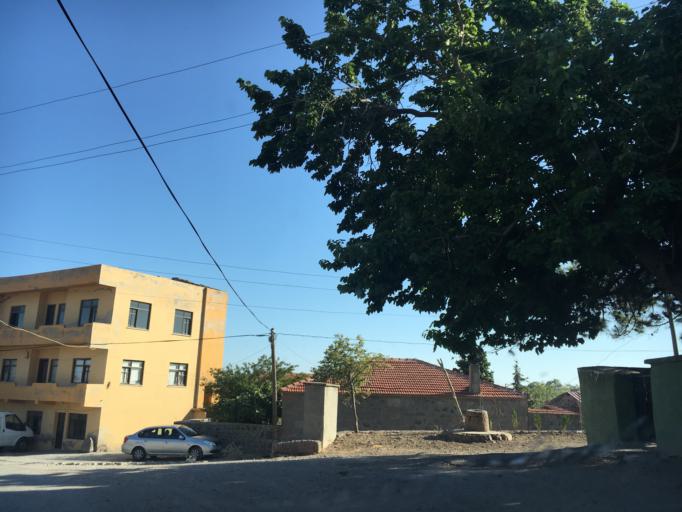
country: TR
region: Canakkale
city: Behram
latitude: 39.5045
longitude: 26.2545
